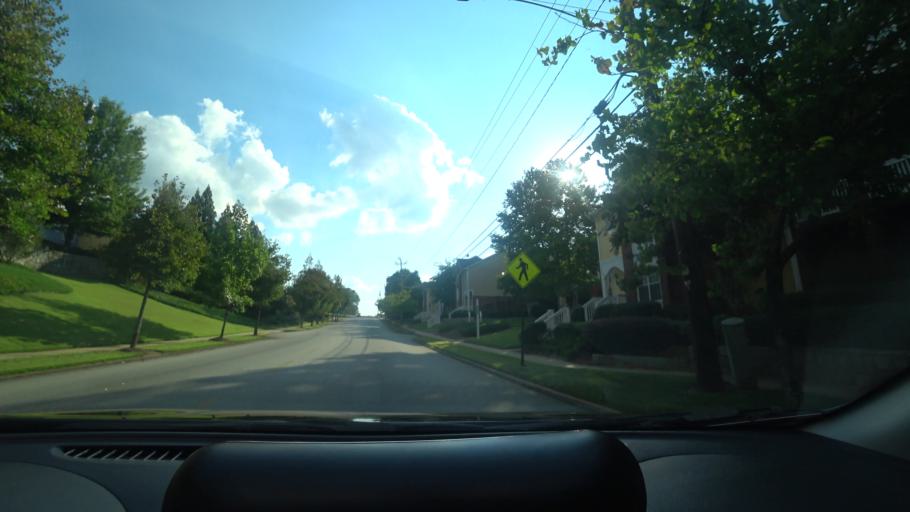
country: US
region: Georgia
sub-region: Fulton County
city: Atlanta
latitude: 33.7084
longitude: -84.3948
